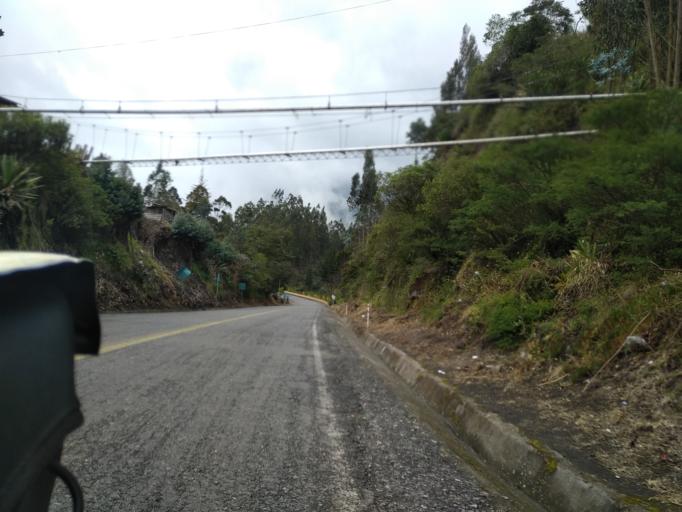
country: EC
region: Chimborazo
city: Guano
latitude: -1.5341
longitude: -78.5243
